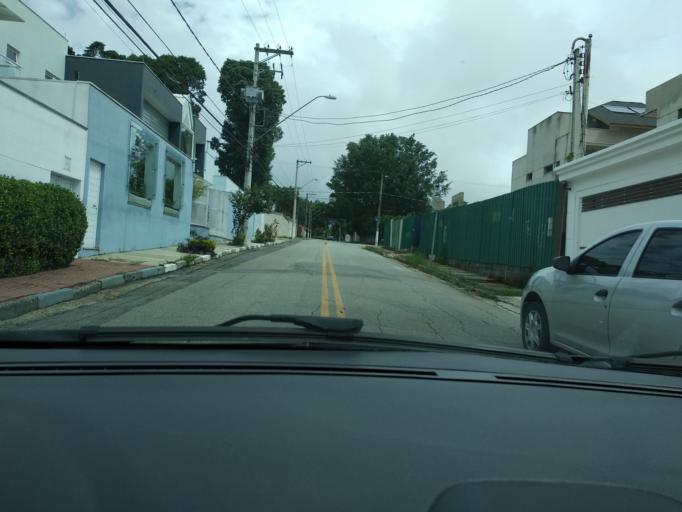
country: BR
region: Sao Paulo
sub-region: Mogi das Cruzes
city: Mogi das Cruzes
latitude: -23.5248
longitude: -46.1763
